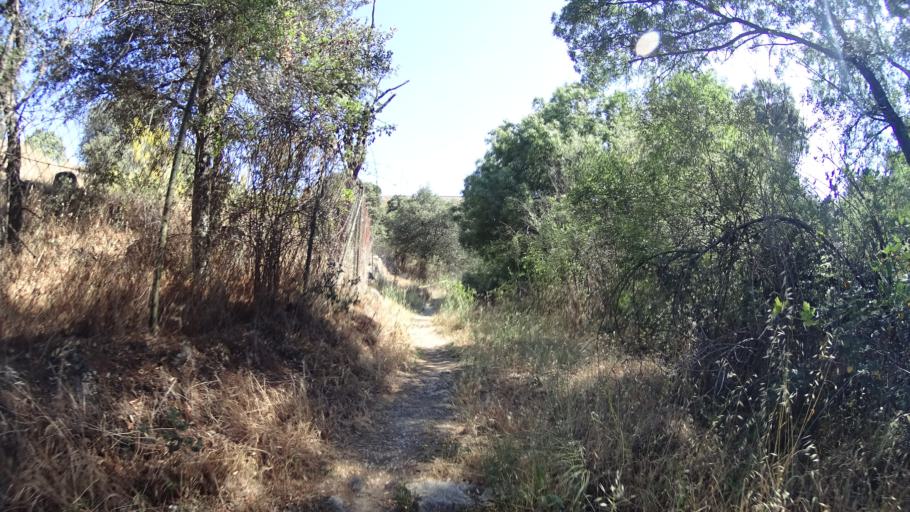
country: ES
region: Madrid
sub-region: Provincia de Madrid
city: Galapagar
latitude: 40.5877
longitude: -3.9671
